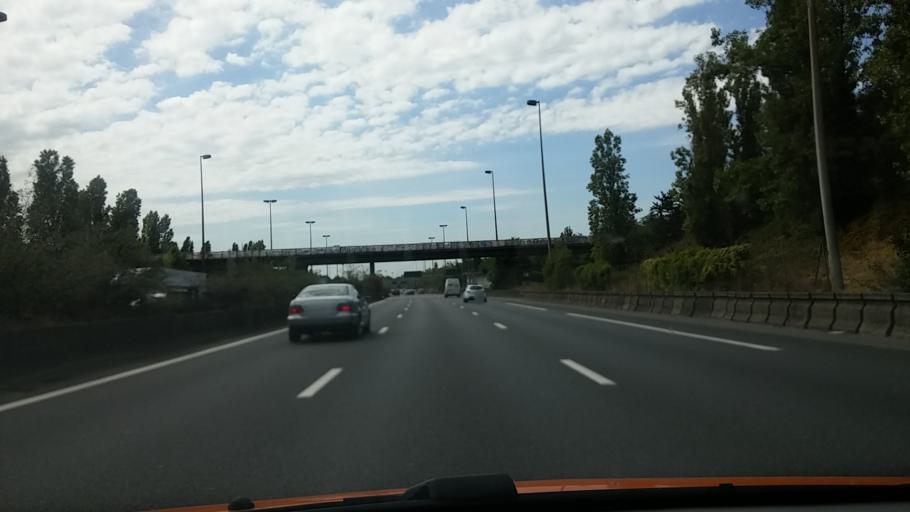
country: FR
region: Ile-de-France
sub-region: Departement du Val-de-Marne
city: Nogent-sur-Marne
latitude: 48.8303
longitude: 2.4884
